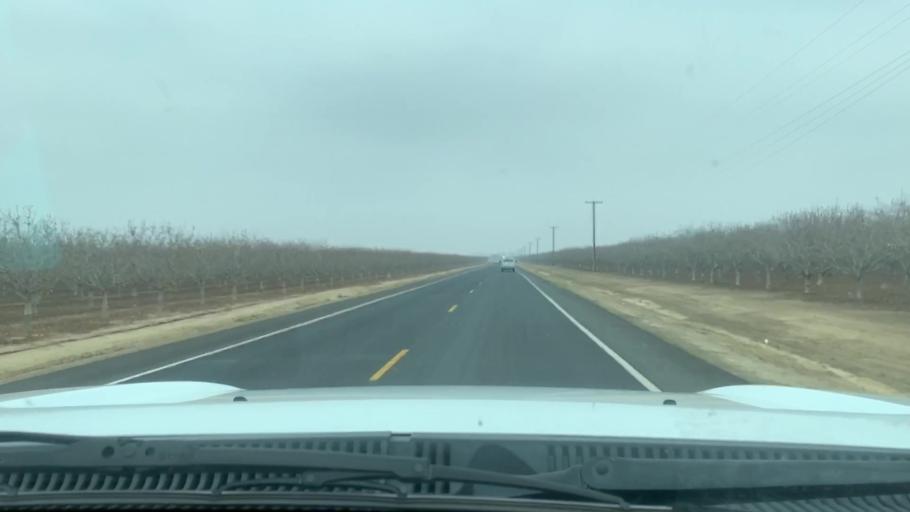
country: US
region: California
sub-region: Kern County
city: Lost Hills
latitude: 35.4993
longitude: -119.6353
